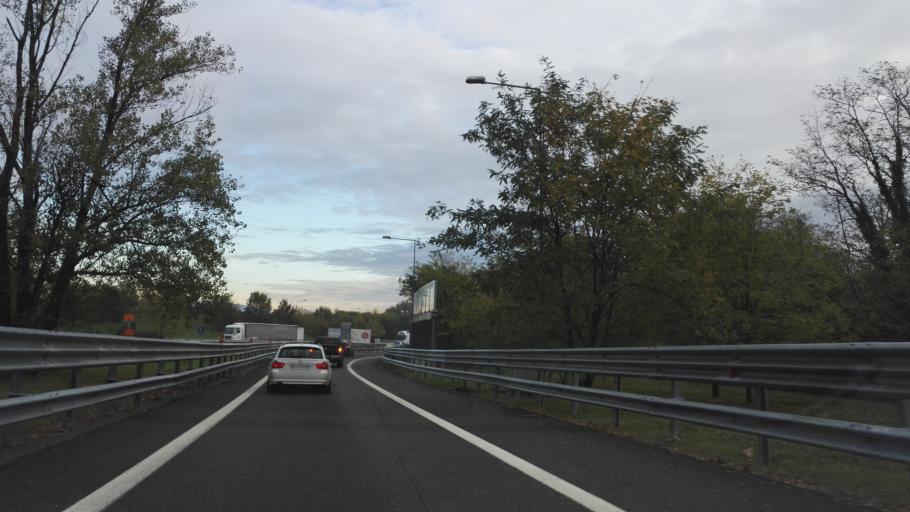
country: IT
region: Lombardy
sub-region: Provincia di Monza e Brianza
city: Agrate Brianza
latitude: 45.5663
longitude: 9.3425
